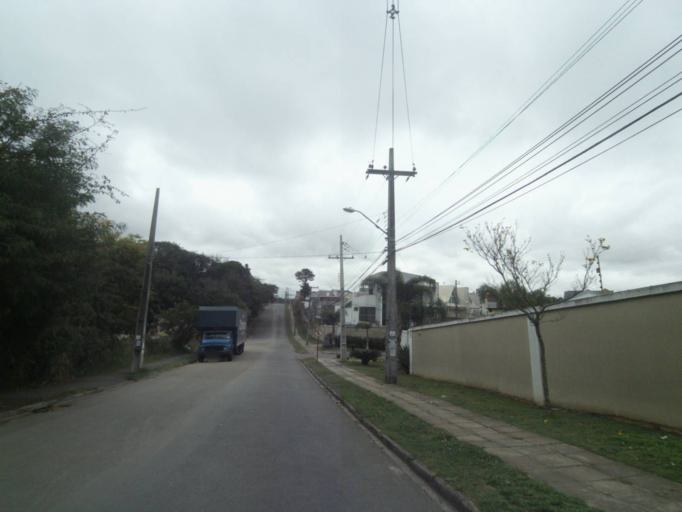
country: BR
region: Parana
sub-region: Curitiba
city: Curitiba
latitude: -25.5066
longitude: -49.2906
